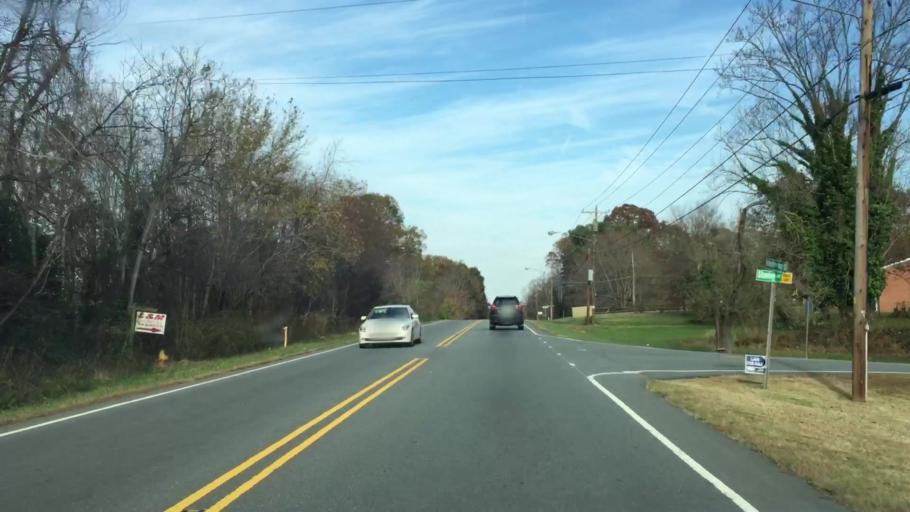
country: US
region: North Carolina
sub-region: Forsyth County
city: Walkertown
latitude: 36.1303
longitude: -80.1723
